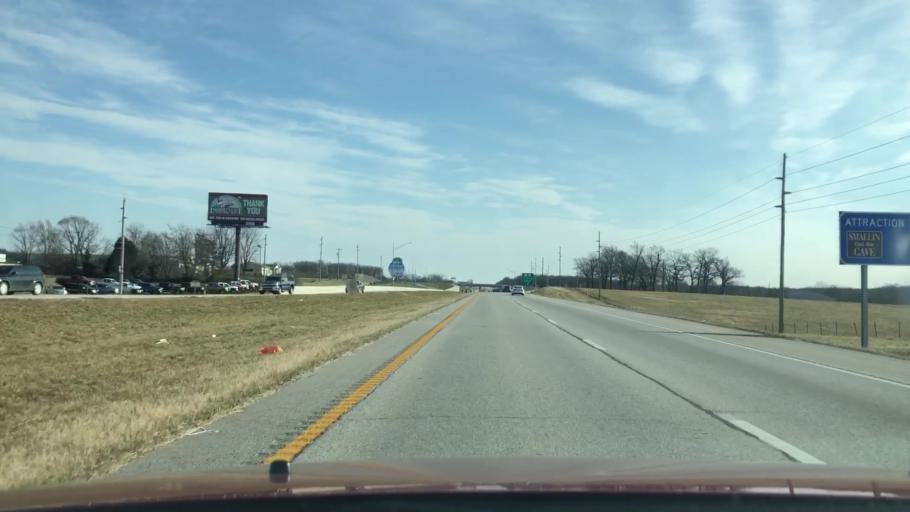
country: US
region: Missouri
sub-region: Christian County
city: Ozark
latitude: 37.1204
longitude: -93.1963
